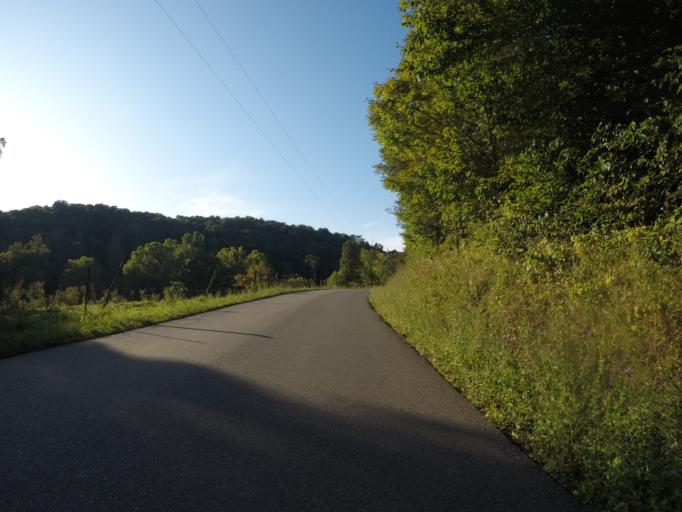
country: US
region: Ohio
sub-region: Lawrence County
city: Coal Grove
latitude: 38.5414
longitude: -82.5500
